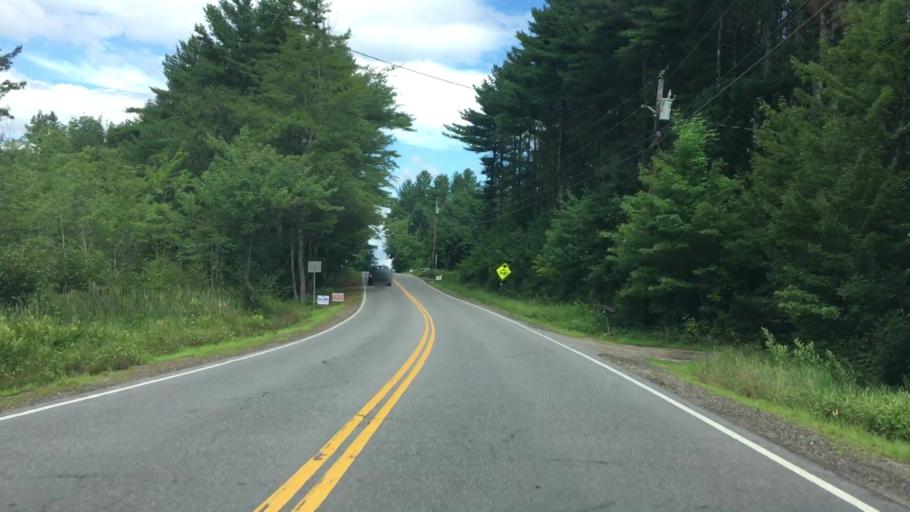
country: US
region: New Hampshire
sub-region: Belknap County
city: Meredith
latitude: 43.5999
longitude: -71.5186
